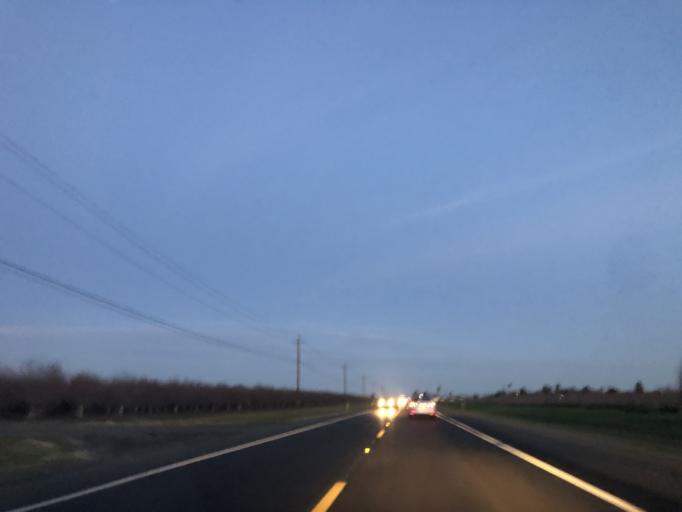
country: US
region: California
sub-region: Yolo County
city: Cottonwood
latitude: 38.6834
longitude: -121.9787
